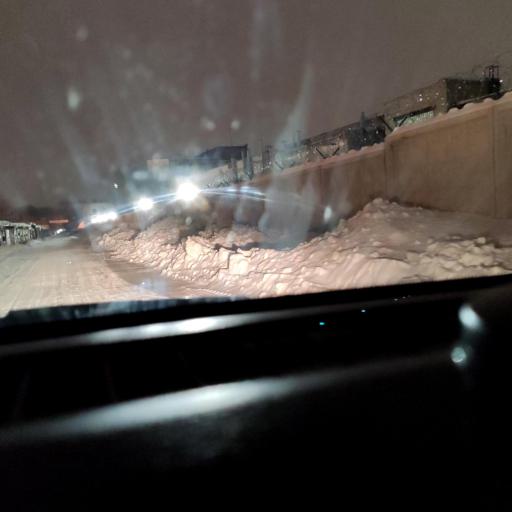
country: RU
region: Perm
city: Froly
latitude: 57.9578
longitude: 56.2483
